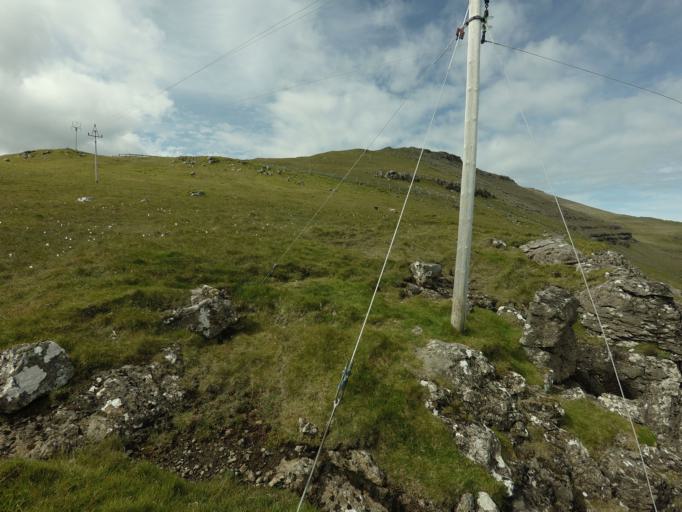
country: FO
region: Nordoyar
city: Klaksvik
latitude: 62.3232
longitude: -6.2846
